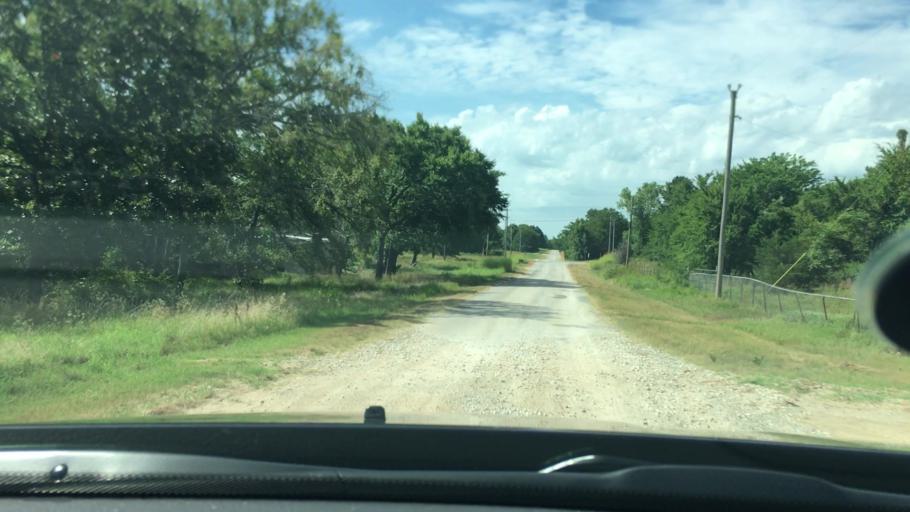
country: US
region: Oklahoma
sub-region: Pontotoc County
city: Ada
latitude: 34.7649
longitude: -96.5651
